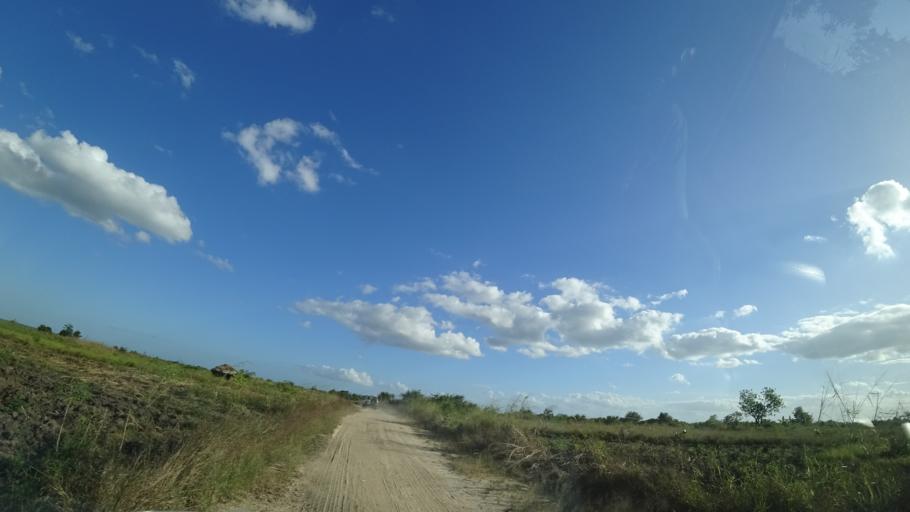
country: MZ
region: Sofala
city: Dondo
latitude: -19.4139
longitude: 34.5663
